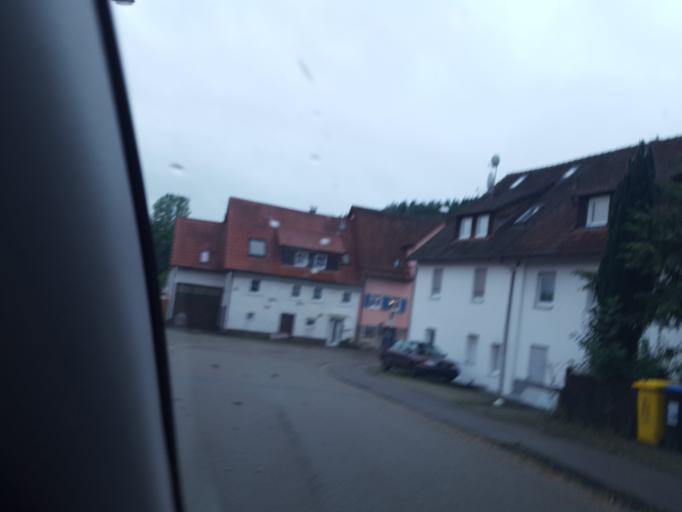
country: DE
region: Baden-Wuerttemberg
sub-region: Regierungsbezirk Stuttgart
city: Rudersberg
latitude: 48.8597
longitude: 9.5291
